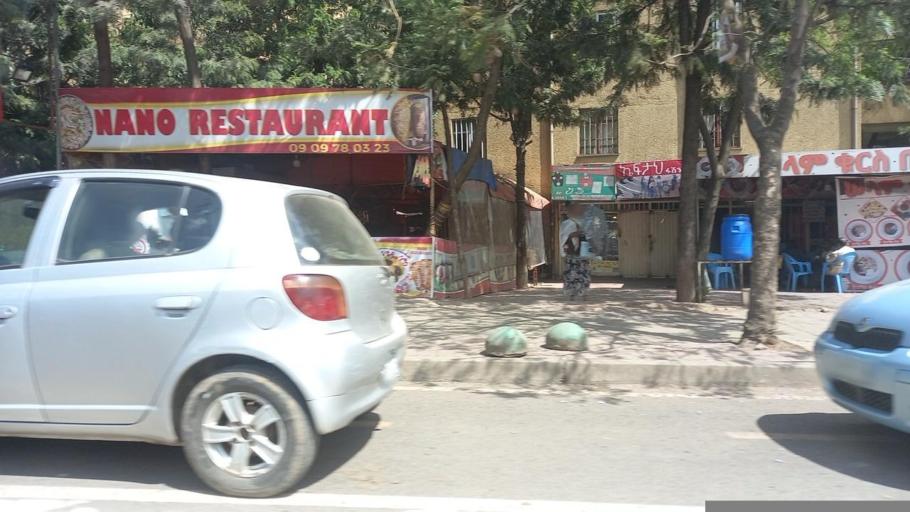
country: ET
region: Adis Abeba
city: Addis Ababa
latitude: 8.9574
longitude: 38.7126
